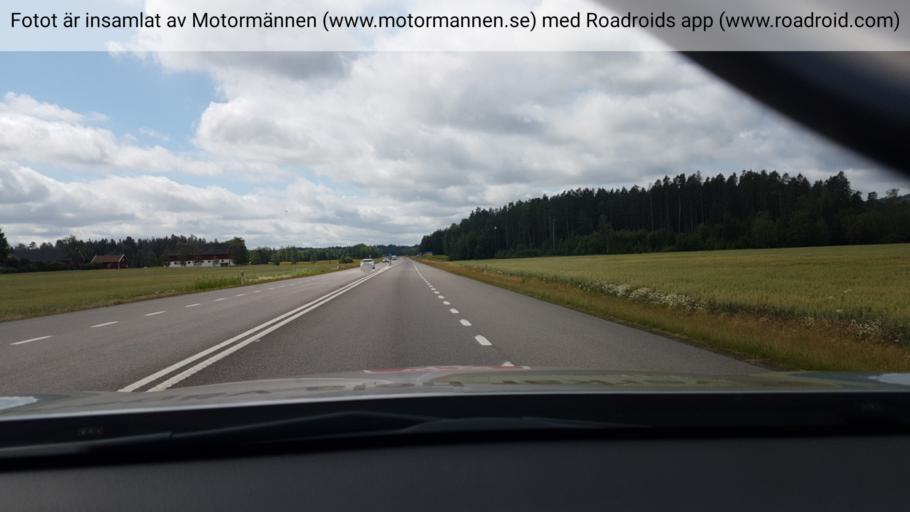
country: SE
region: Vaestra Goetaland
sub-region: Grastorps Kommun
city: Graestorp
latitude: 58.3121
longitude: 12.5580
